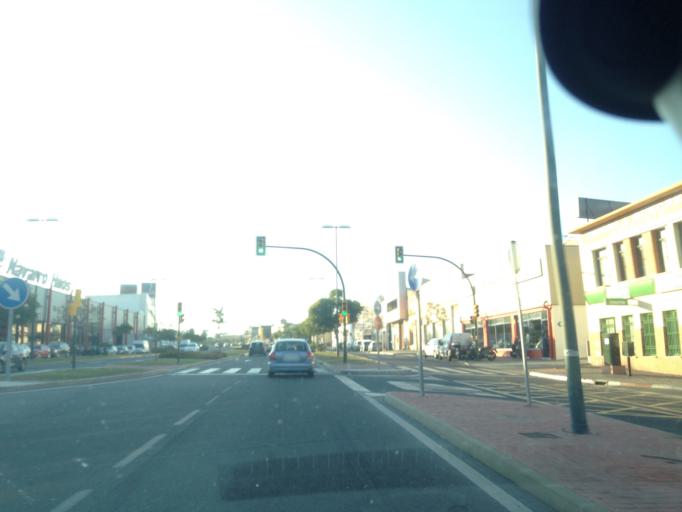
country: ES
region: Andalusia
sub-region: Provincia de Malaga
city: Malaga
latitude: 36.7075
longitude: -4.4750
